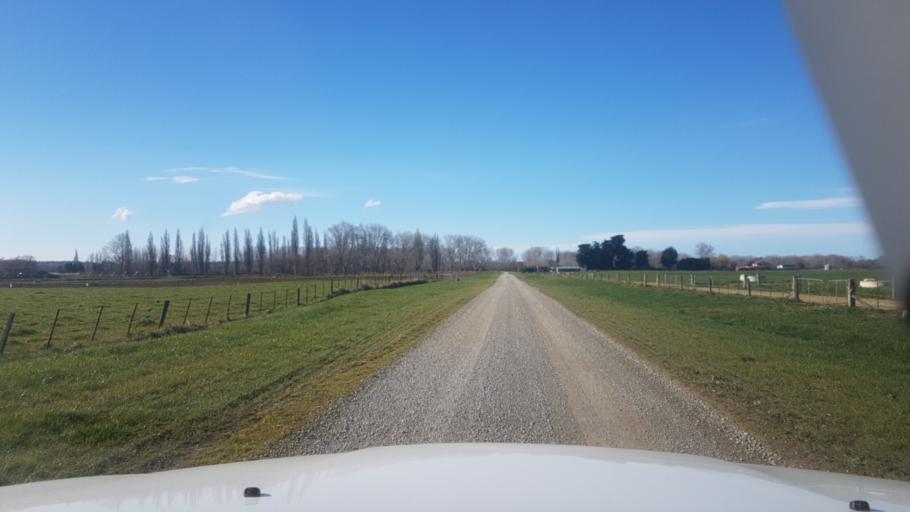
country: NZ
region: Canterbury
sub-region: Timaru District
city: Pleasant Point
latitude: -44.2511
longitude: 171.1115
